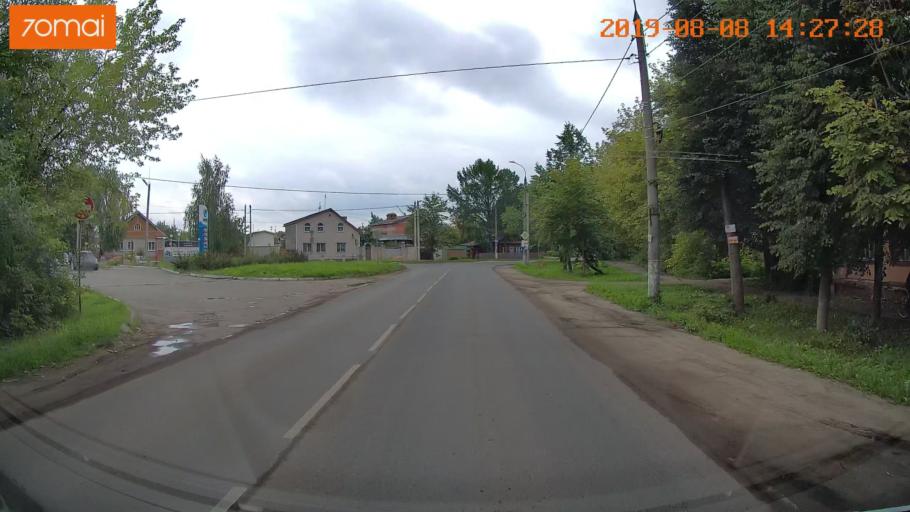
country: RU
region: Ivanovo
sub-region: Gorod Ivanovo
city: Ivanovo
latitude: 56.9970
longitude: 40.9412
